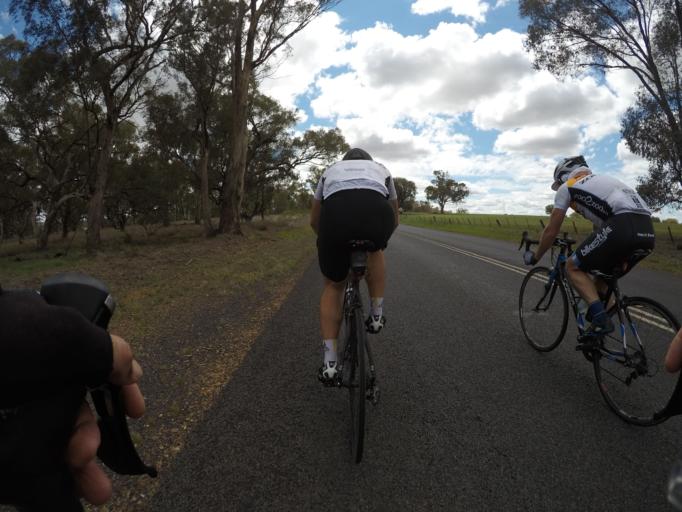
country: AU
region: New South Wales
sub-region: Dubbo Municipality
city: Dubbo
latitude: -32.4749
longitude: 148.5641
